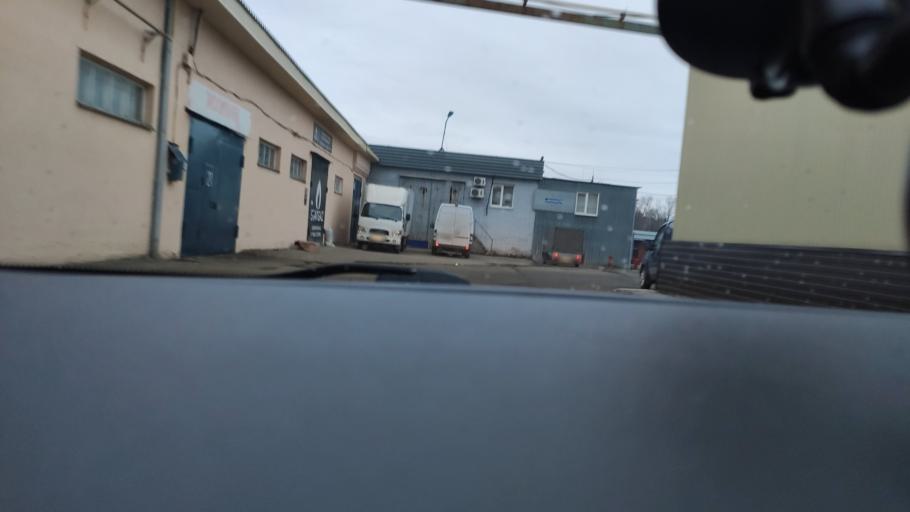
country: RU
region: Perm
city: Froly
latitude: 57.9557
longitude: 56.2245
